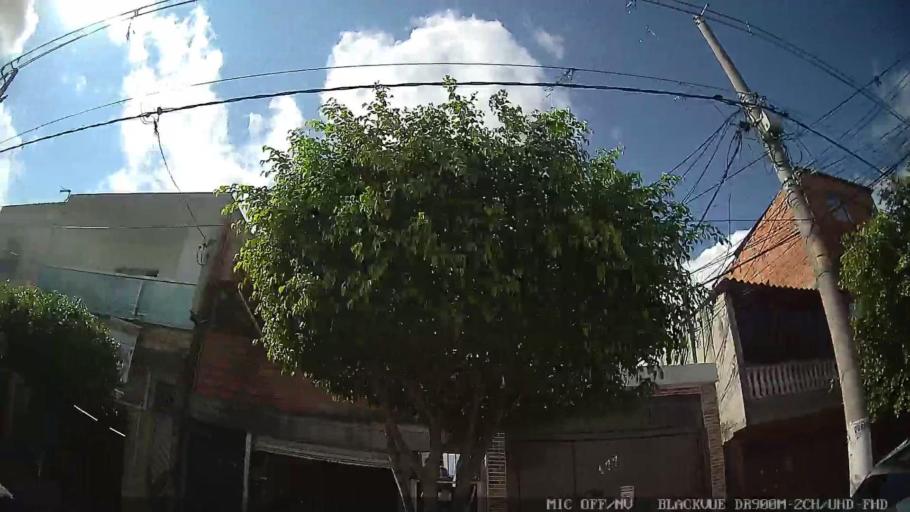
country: BR
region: Sao Paulo
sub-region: Guarulhos
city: Guarulhos
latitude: -23.4865
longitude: -46.4828
